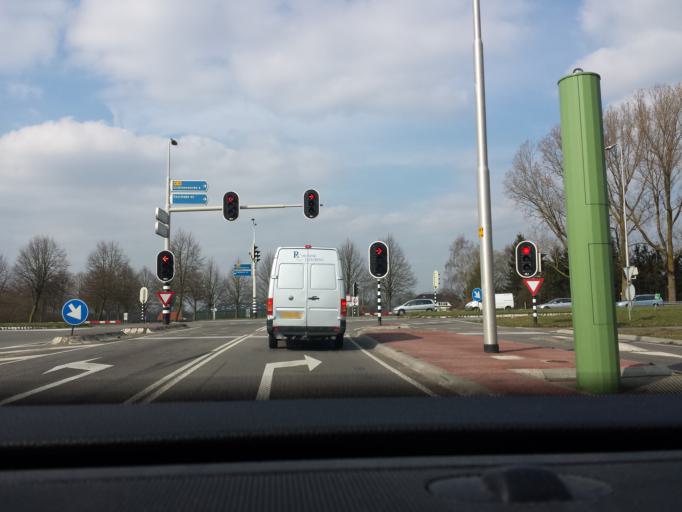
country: NL
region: Gelderland
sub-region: Oude IJsselstreek
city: Varsseveld
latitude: 51.9525
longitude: 6.4696
